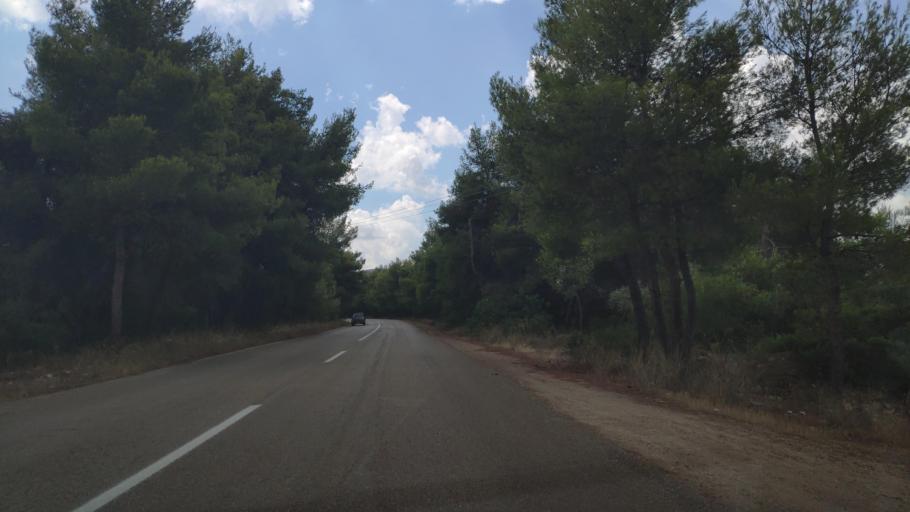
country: GR
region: Central Greece
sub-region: Nomos Fthiotidos
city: Malesina
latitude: 38.6235
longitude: 23.1803
